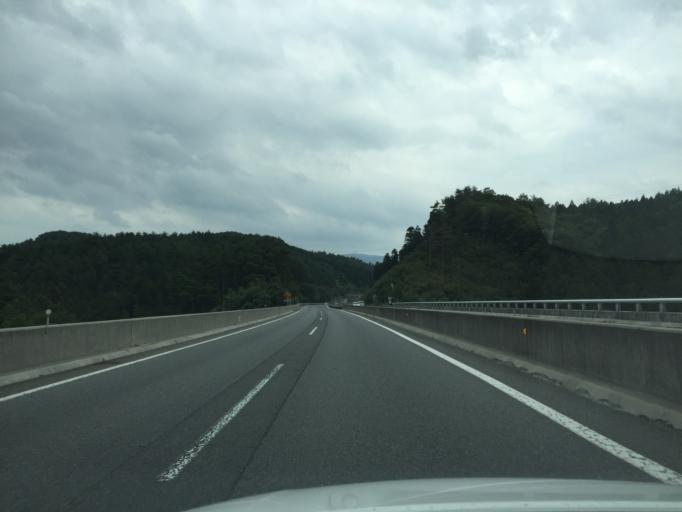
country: JP
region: Fukushima
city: Iwaki
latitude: 37.1529
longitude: 140.7363
